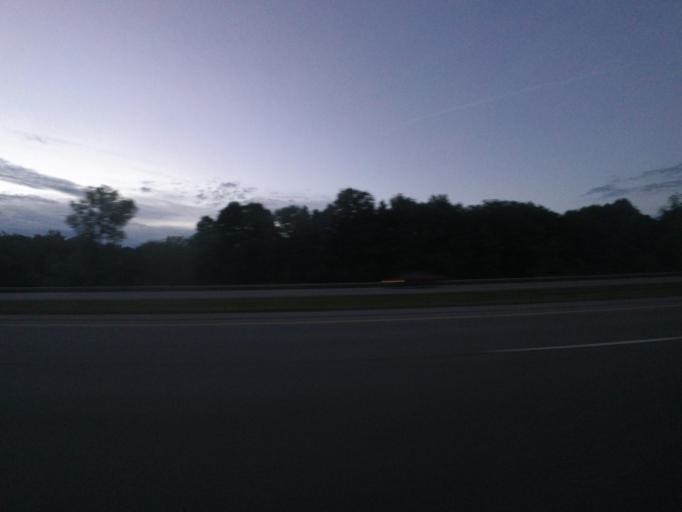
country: US
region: Ohio
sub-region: Richland County
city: Lincoln Heights
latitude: 40.7966
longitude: -82.3953
